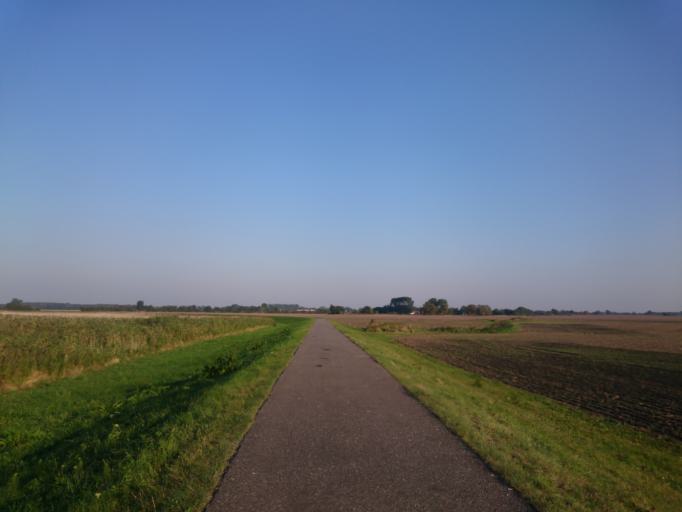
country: DE
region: Mecklenburg-Vorpommern
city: Velgast
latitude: 54.3507
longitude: 12.8412
